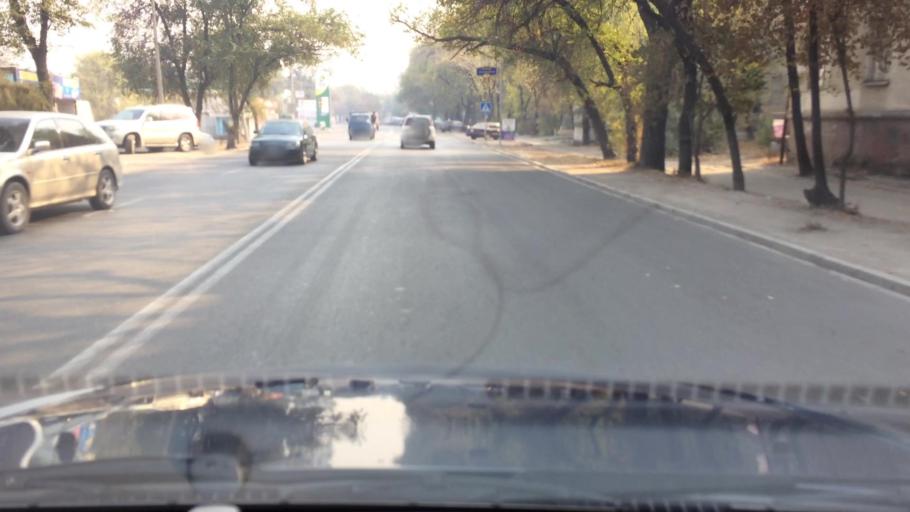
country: KG
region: Chuy
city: Bishkek
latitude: 42.8627
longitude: 74.6063
